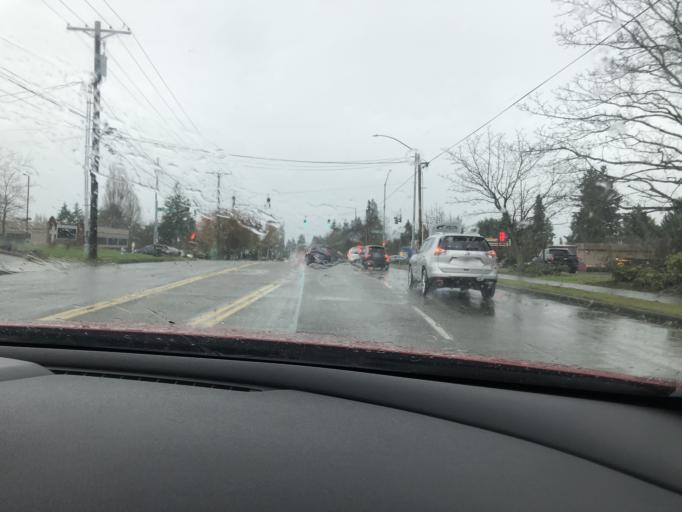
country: US
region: Washington
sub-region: Pierce County
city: Tacoma
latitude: 47.2426
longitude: -122.4675
